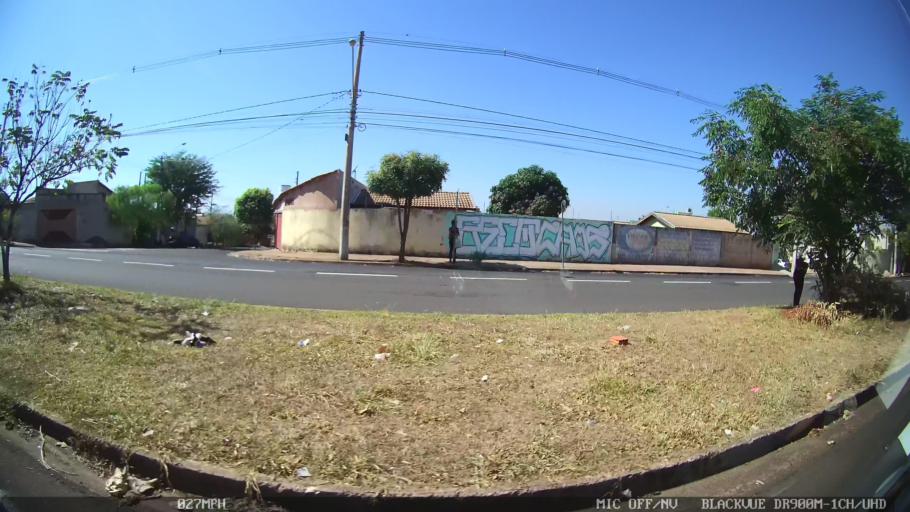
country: BR
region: Sao Paulo
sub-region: Sao Jose Do Rio Preto
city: Sao Jose do Rio Preto
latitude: -20.7449
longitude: -49.4086
